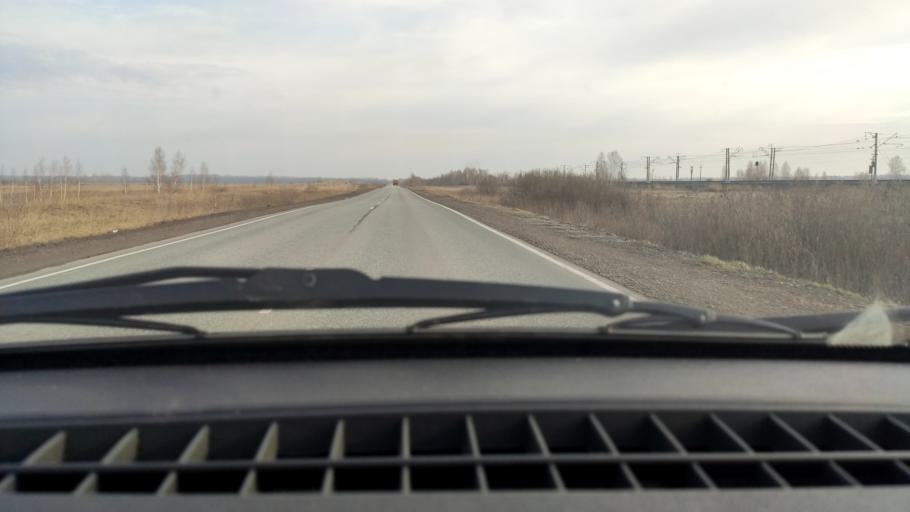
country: RU
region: Bashkortostan
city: Chishmy
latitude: 54.4199
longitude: 55.2277
